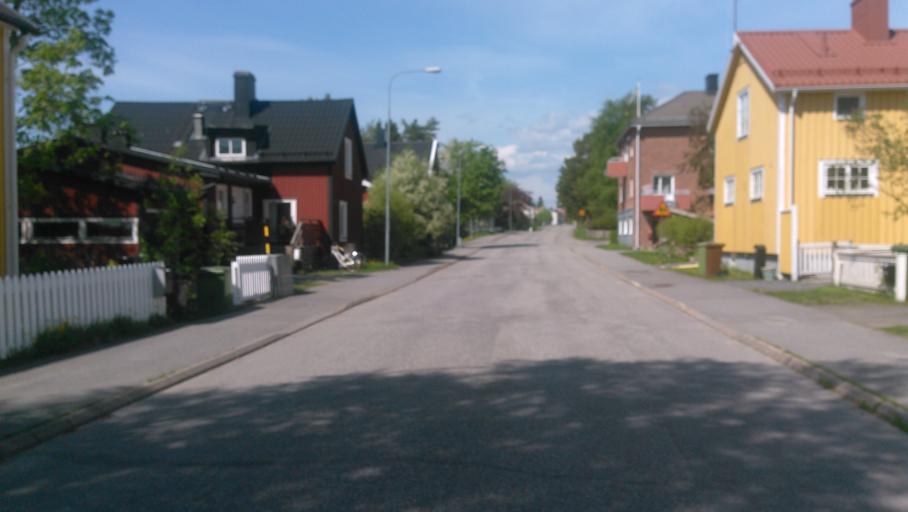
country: SE
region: Vaesterbotten
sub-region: Umea Kommun
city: Umea
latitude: 63.8070
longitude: 20.3017
